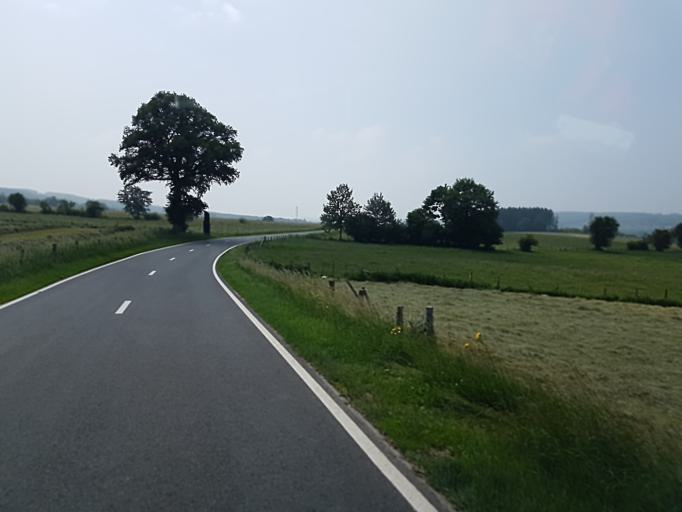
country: BE
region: Wallonia
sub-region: Province du Luxembourg
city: Manhay
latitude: 50.3120
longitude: 5.7243
